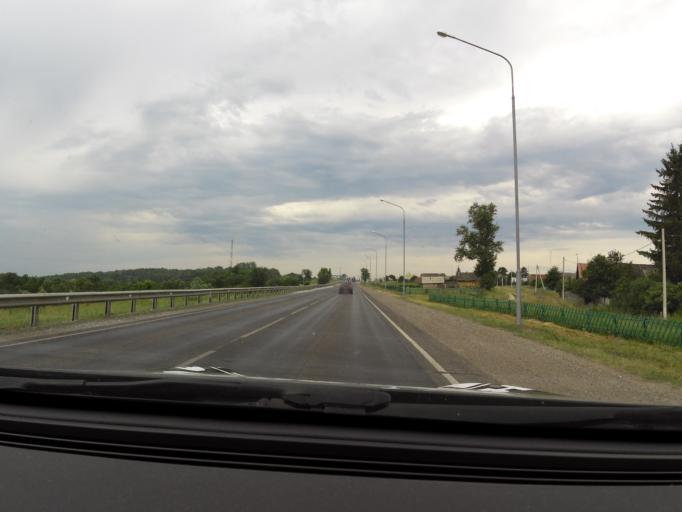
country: RU
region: Bashkortostan
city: Urman
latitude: 54.8230
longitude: 56.8867
